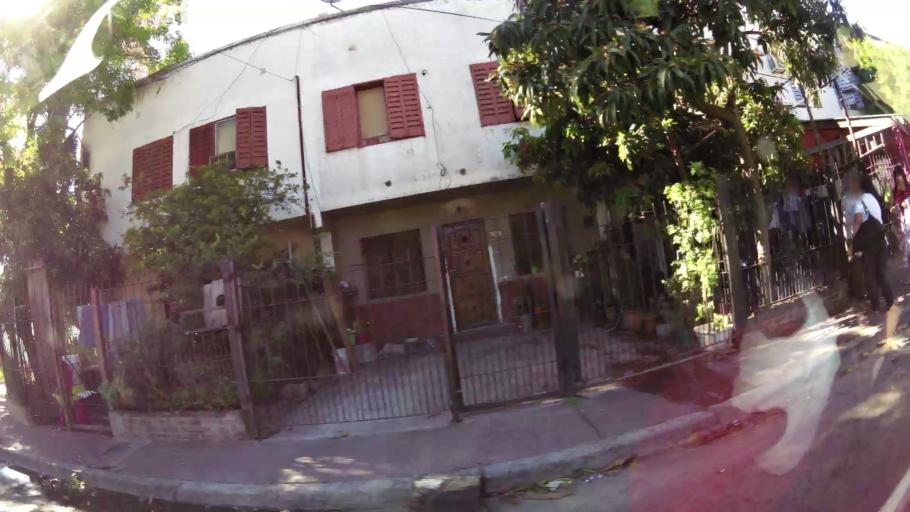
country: AR
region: Buenos Aires
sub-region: Partido de General San Martin
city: General San Martin
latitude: -34.5466
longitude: -58.5236
